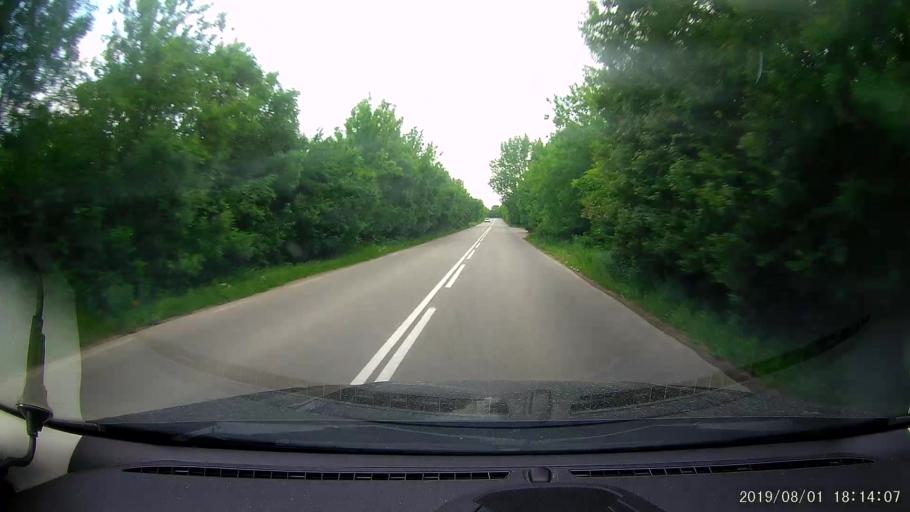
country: BG
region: Silistra
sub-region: Obshtina Dulovo
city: Dulovo
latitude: 43.7755
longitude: 27.1287
